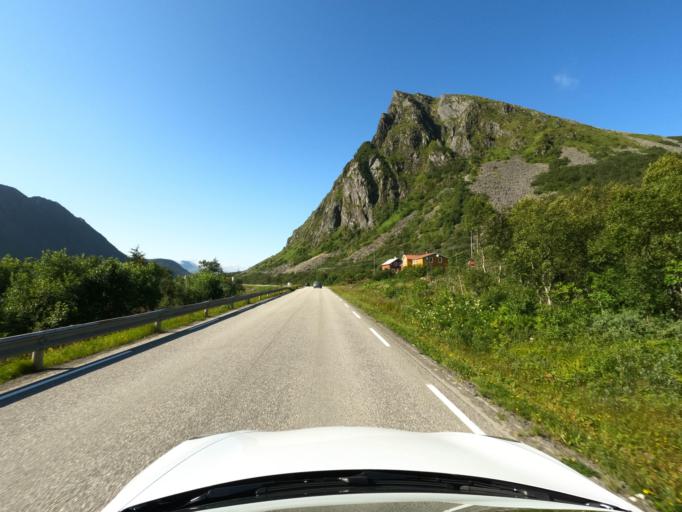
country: NO
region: Nordland
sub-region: Vagan
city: Kabelvag
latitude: 68.2603
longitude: 14.1939
